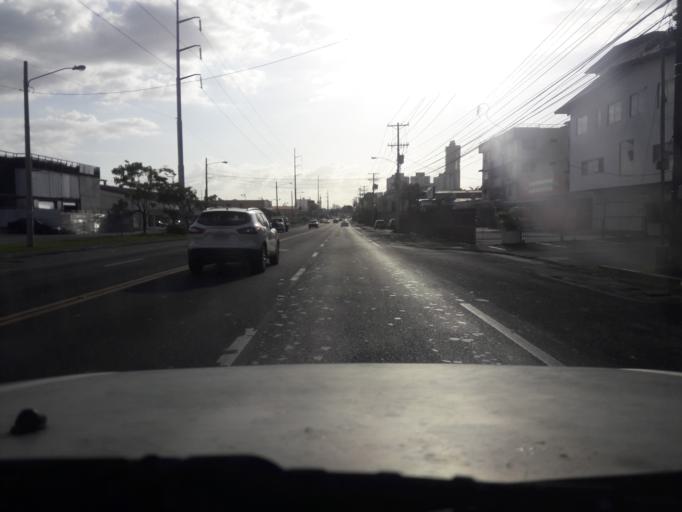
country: PA
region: Panama
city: San Miguelito
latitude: 9.0297
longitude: -79.4773
